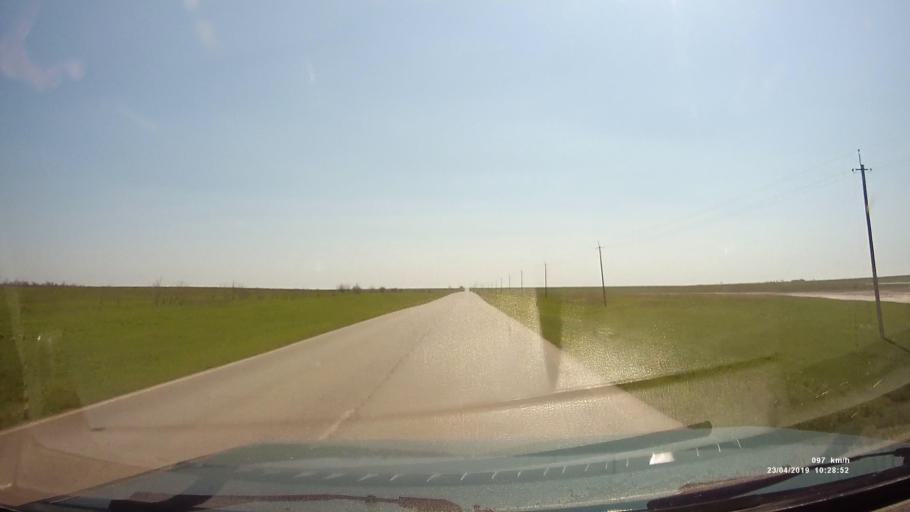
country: RU
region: Kalmykiya
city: Yashalta
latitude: 46.6024
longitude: 42.5158
